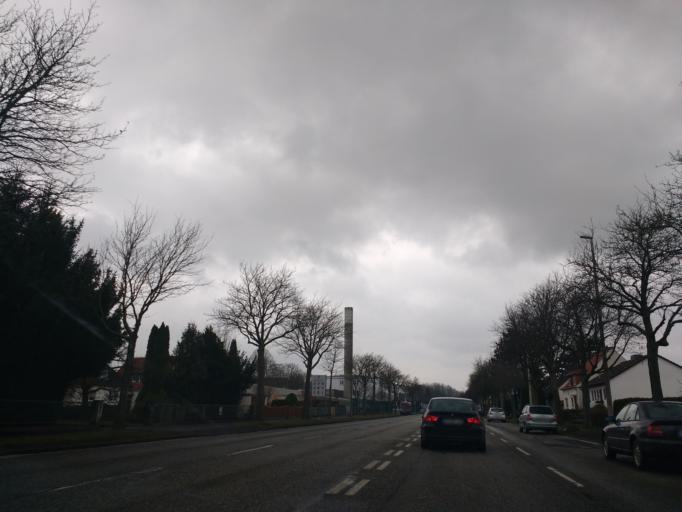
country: DE
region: Hesse
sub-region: Regierungsbezirk Kassel
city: Fuldabruck
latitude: 51.2789
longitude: 9.4641
